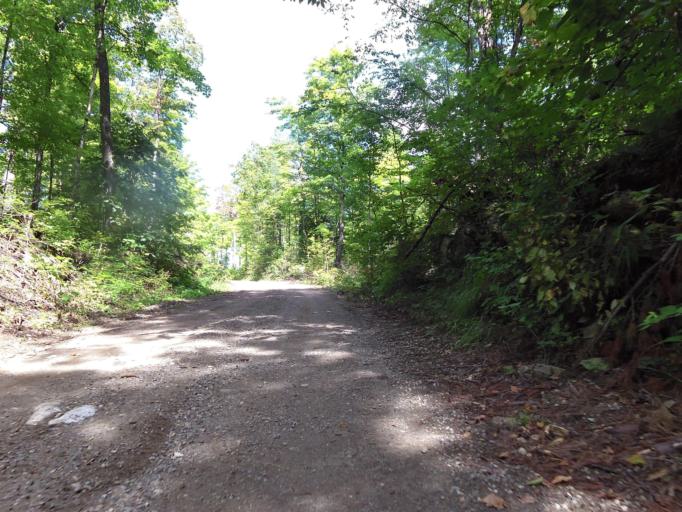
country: CA
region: Ontario
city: Renfrew
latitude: 45.1271
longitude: -76.7193
